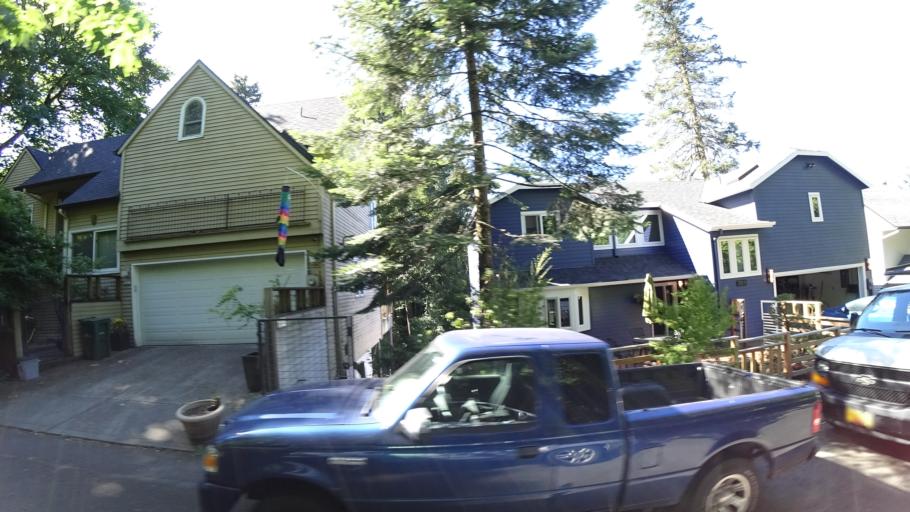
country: US
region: Oregon
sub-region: Multnomah County
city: Portland
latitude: 45.5312
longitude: -122.7128
